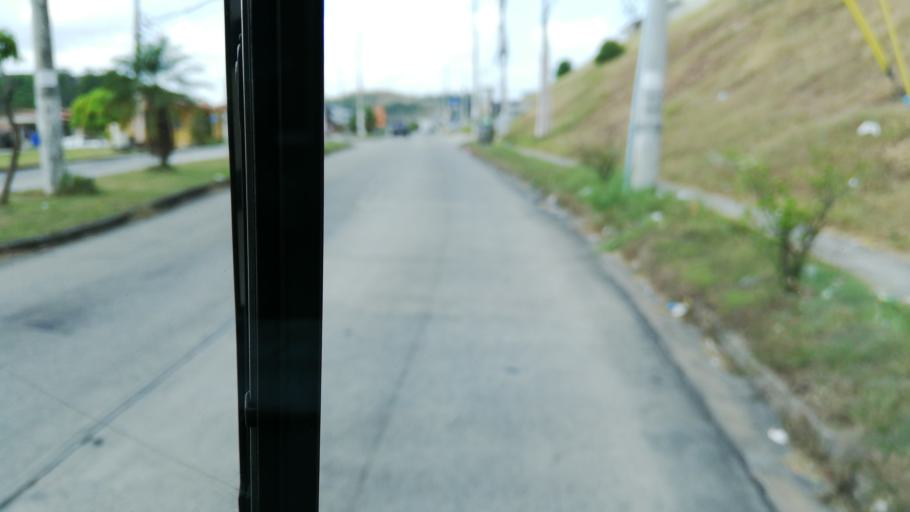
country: PA
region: Panama
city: San Miguelito
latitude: 9.0711
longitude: -79.4569
